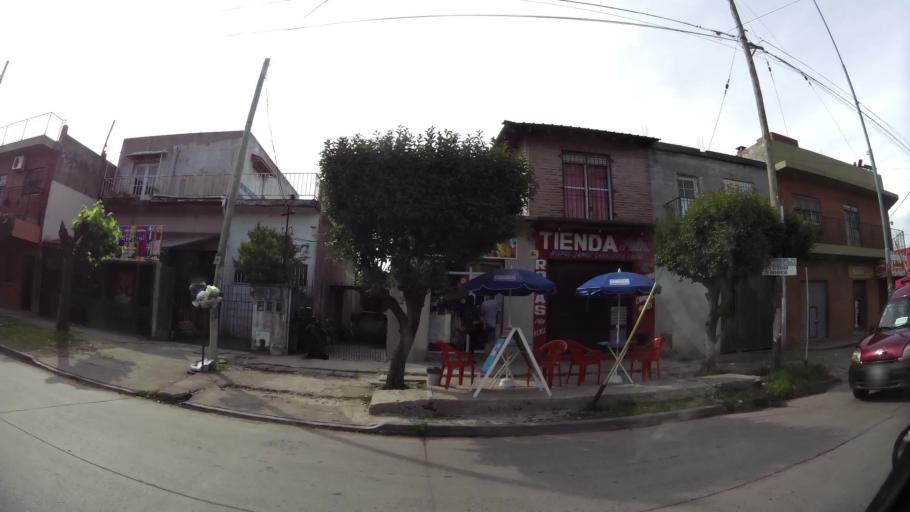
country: AR
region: Buenos Aires
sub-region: Partido de Quilmes
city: Quilmes
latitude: -34.7684
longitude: -58.2572
